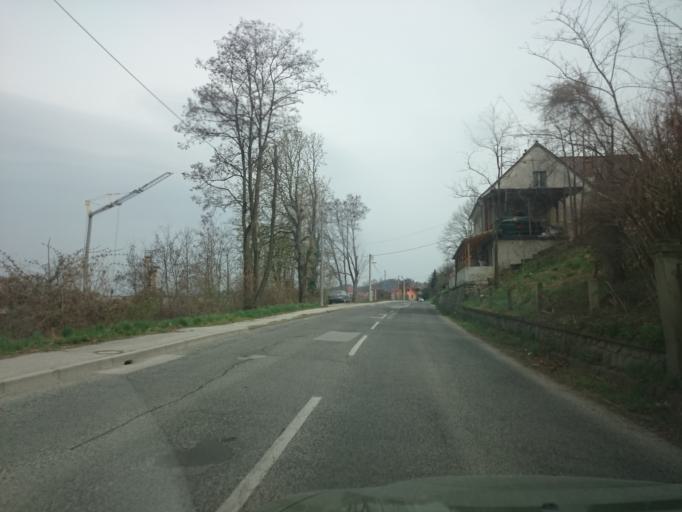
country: SI
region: Celje
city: Celje
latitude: 46.2313
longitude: 15.2831
